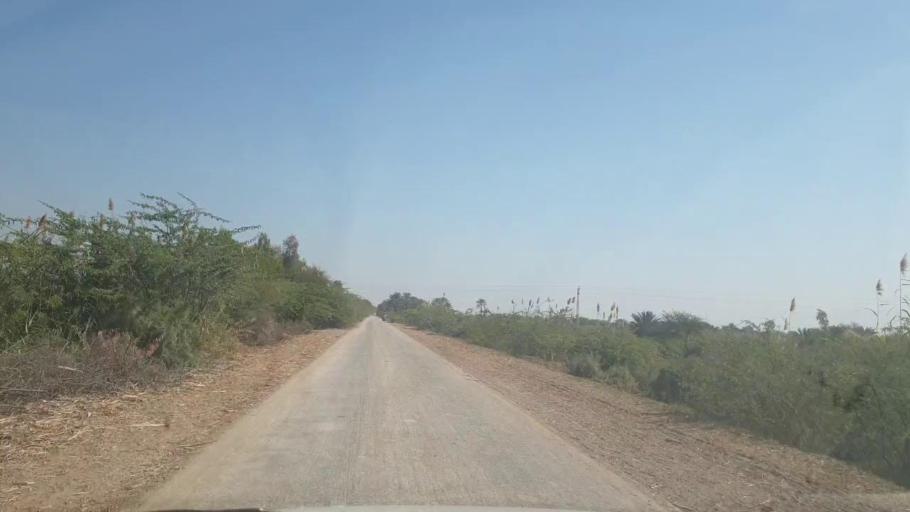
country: PK
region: Sindh
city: Mirpur Khas
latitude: 25.5146
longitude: 69.1737
